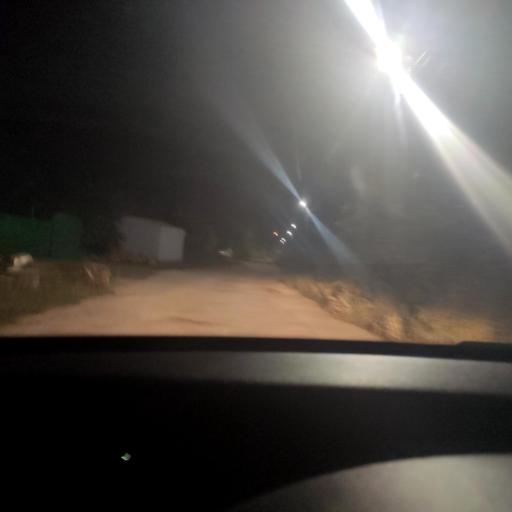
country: RU
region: Samara
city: Samara
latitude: 53.2251
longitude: 50.2175
